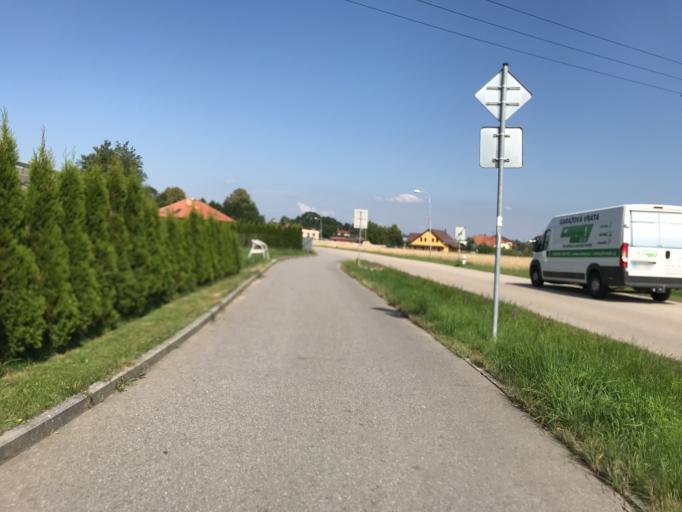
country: CZ
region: Jihocesky
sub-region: Okres Jindrichuv Hradec
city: Trebon
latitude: 49.0157
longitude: 14.7510
